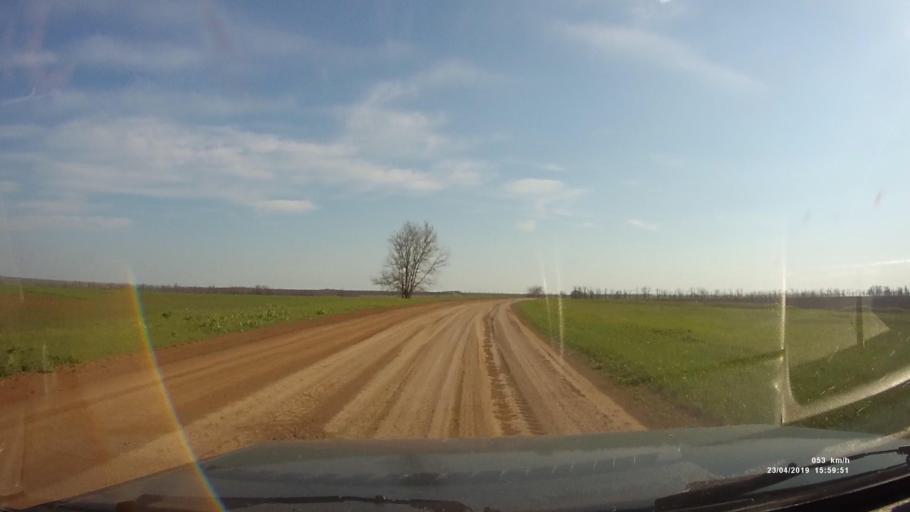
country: RU
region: Rostov
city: Remontnoye
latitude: 46.5136
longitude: 43.1094
